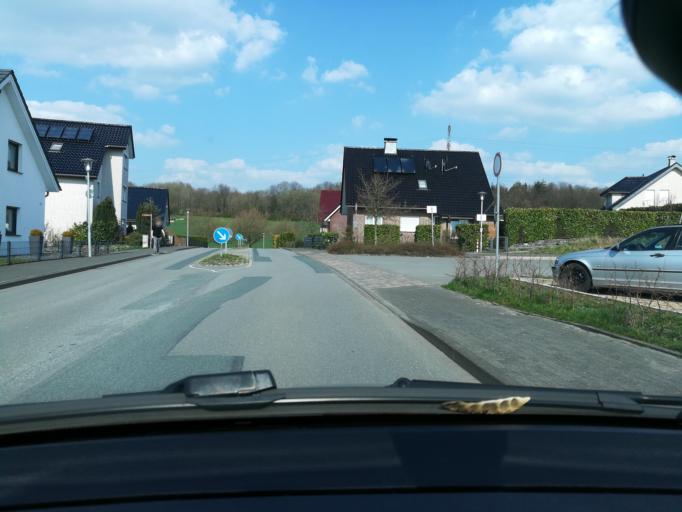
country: DE
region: North Rhine-Westphalia
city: Borgholzhausen
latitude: 52.1033
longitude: 8.3117
